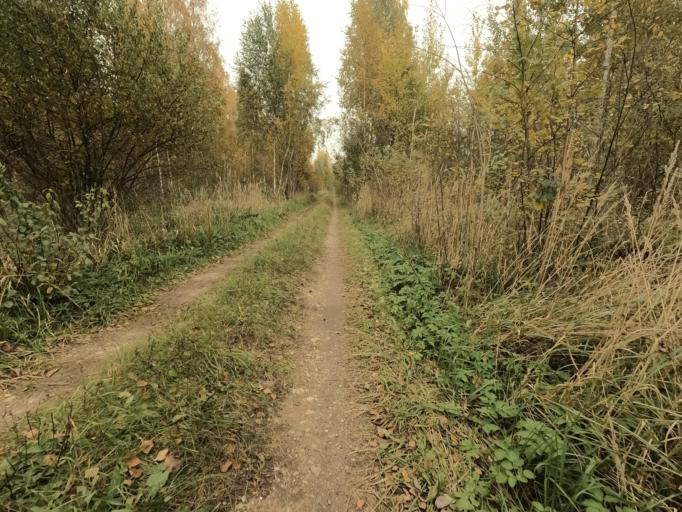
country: RU
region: Novgorod
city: Pankovka
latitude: 58.8763
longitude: 30.9403
